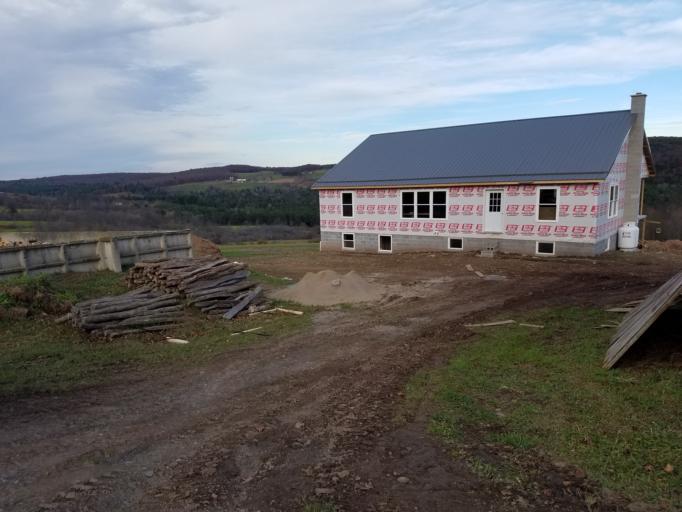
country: US
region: New York
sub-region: Delaware County
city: Sidney
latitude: 42.4117
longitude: -75.4367
